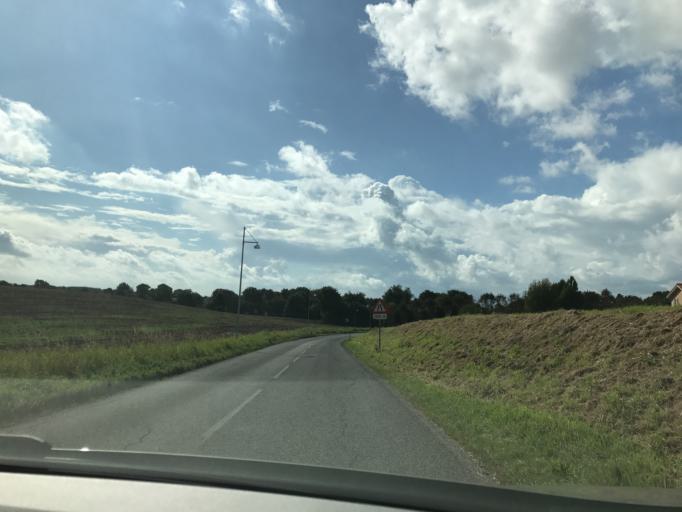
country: DK
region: South Denmark
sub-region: Middelfart Kommune
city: Norre Aby
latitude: 55.4668
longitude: 9.8044
